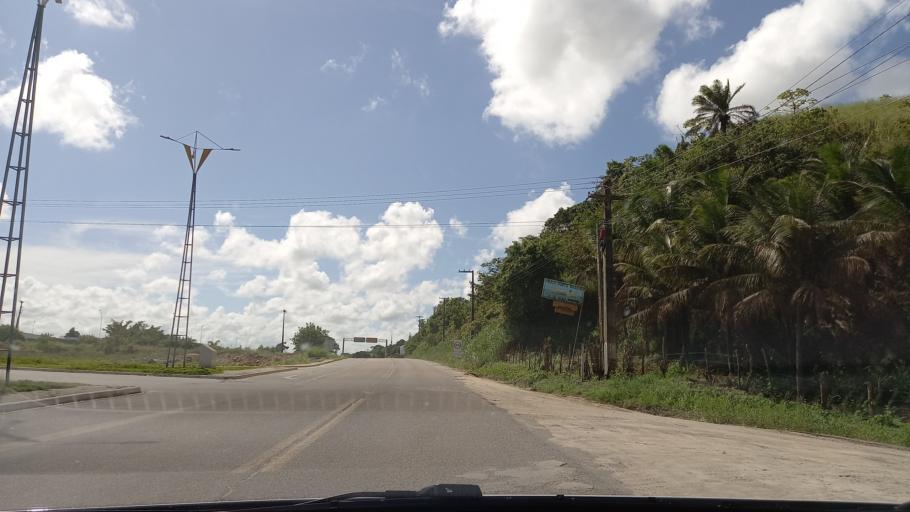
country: BR
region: Pernambuco
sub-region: Barreiros
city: Barreiros
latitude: -8.8082
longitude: -35.1846
